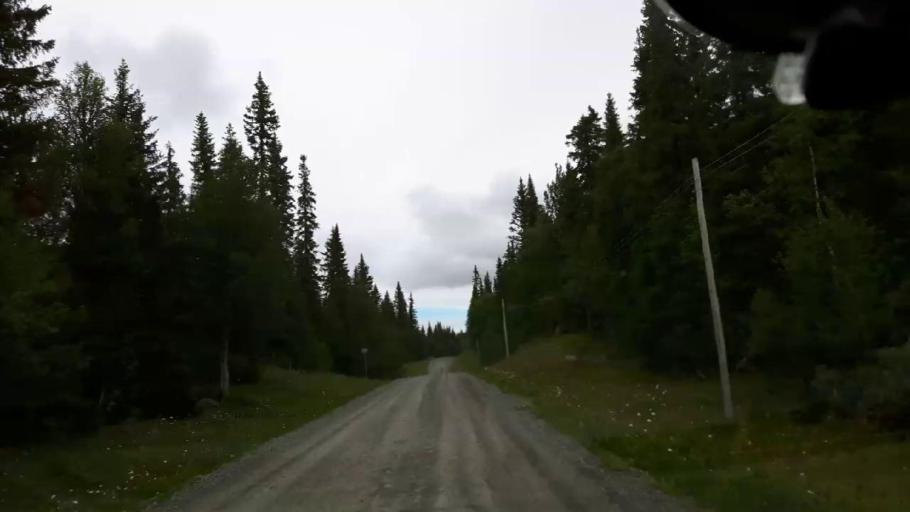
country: SE
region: Jaemtland
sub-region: Krokoms Kommun
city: Valla
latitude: 63.7448
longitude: 13.8361
